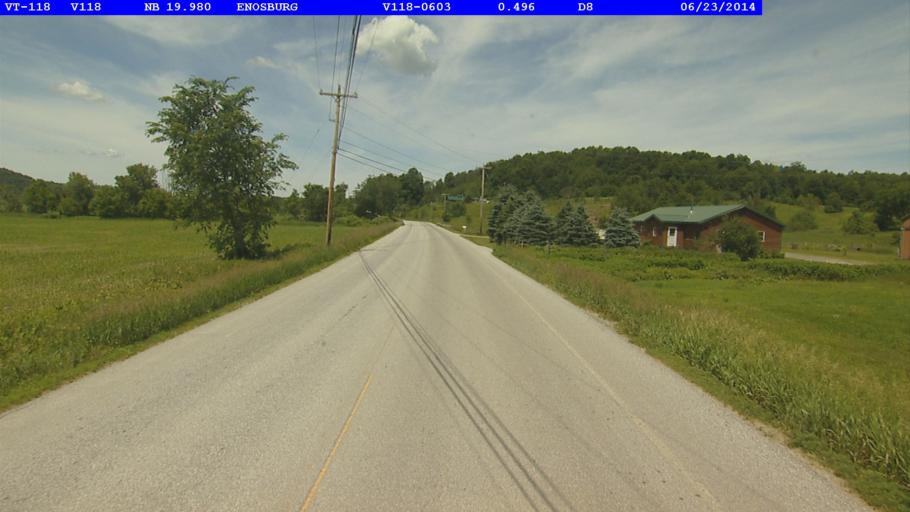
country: US
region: Vermont
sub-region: Franklin County
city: Richford
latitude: 44.9266
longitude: -72.6784
